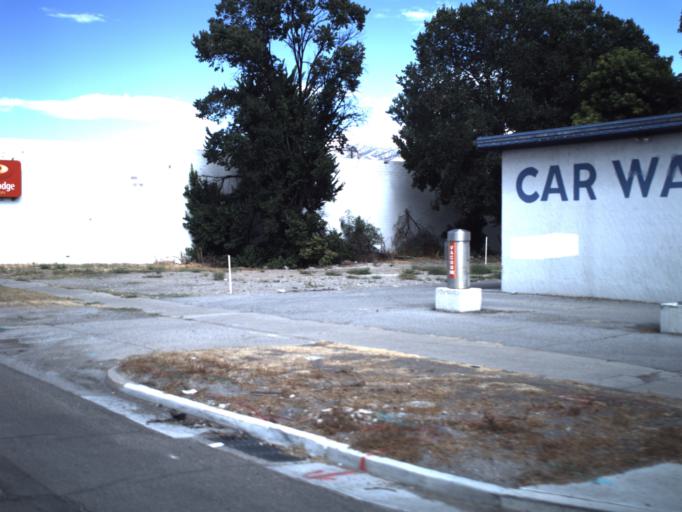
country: US
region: Utah
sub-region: Cache County
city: Logan
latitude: 41.7241
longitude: -111.8351
